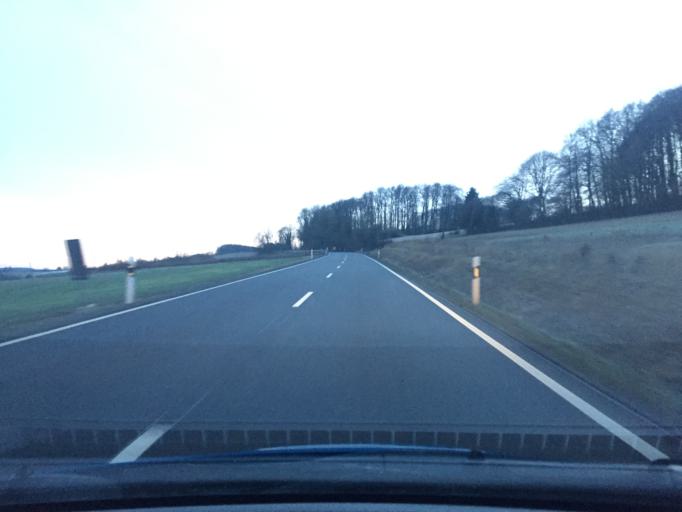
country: DE
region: Lower Saxony
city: Luerdissen
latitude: 51.9683
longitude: 9.6515
